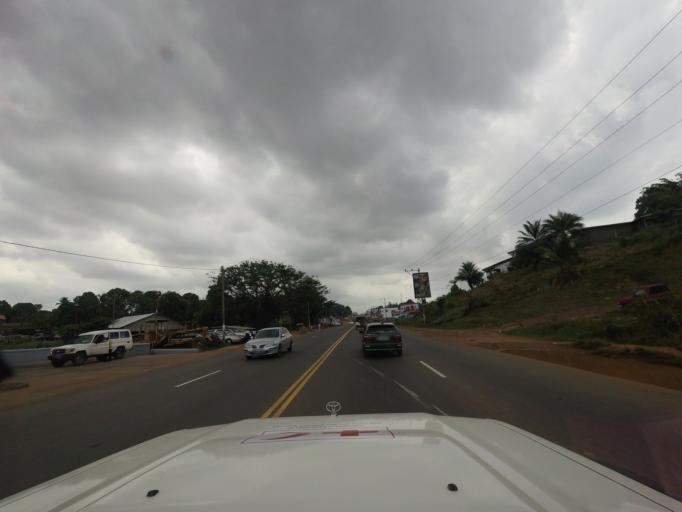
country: LR
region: Montserrado
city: Monrovia
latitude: 6.2645
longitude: -10.7109
